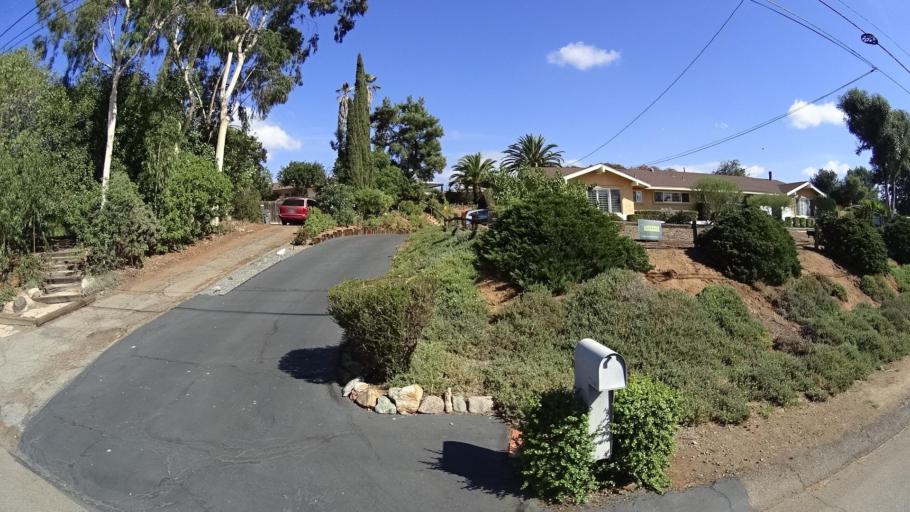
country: US
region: California
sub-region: San Diego County
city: Casa de Oro-Mount Helix
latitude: 32.7631
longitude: -116.9493
